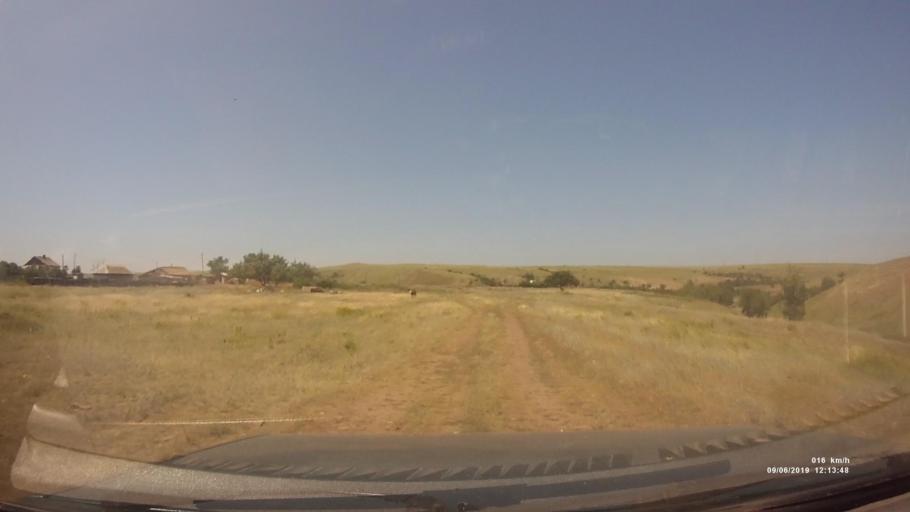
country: RU
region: Rostov
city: Staraya Stanitsa
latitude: 48.2512
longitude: 40.3261
